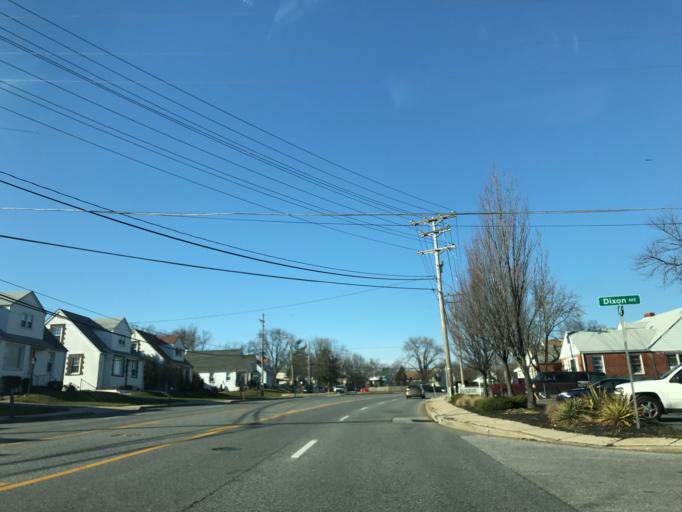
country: US
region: Maryland
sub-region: Baltimore County
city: Carney
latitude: 39.3957
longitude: -76.5273
